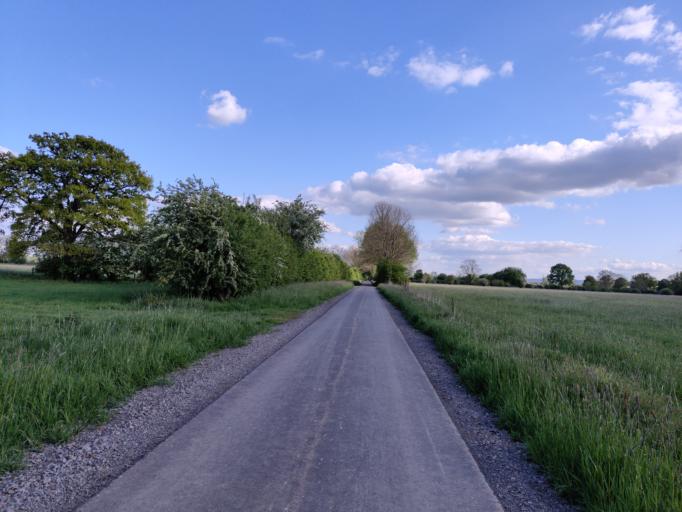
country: DE
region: Lower Saxony
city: Wunstorf
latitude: 52.4453
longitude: 9.4729
